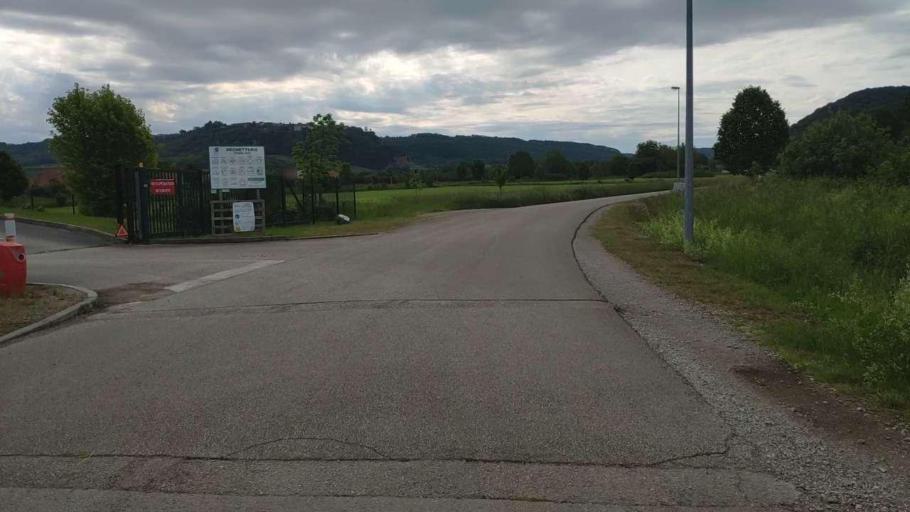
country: FR
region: Franche-Comte
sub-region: Departement du Jura
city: Perrigny
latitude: 46.7574
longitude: 5.5990
